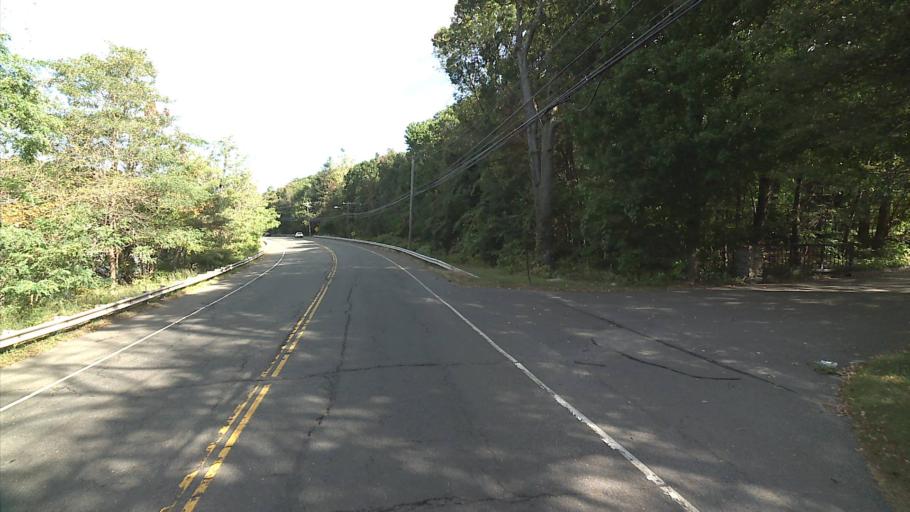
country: US
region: Connecticut
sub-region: Hartford County
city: Bristol
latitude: 41.6476
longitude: -72.9637
